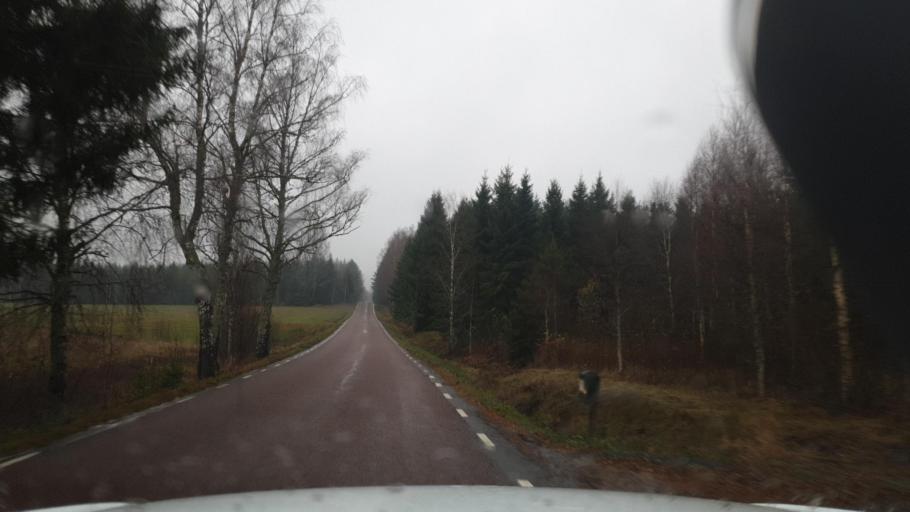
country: SE
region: Vaermland
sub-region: Karlstads Kommun
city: Edsvalla
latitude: 59.5144
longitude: 13.1103
